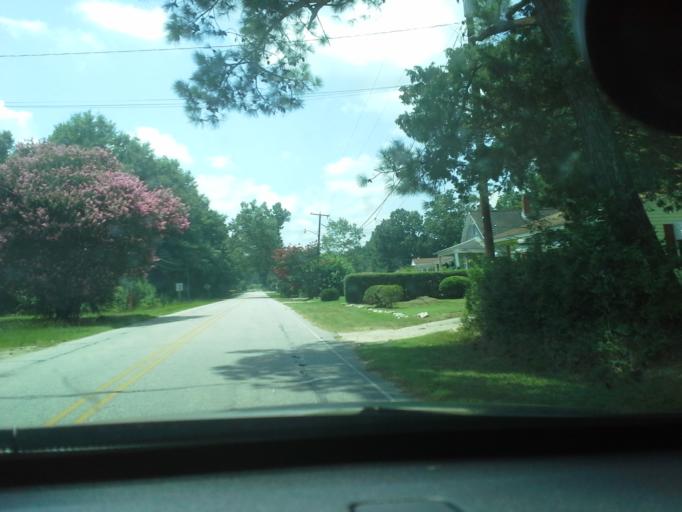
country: US
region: North Carolina
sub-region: Washington County
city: Plymouth
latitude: 35.8506
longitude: -76.7583
